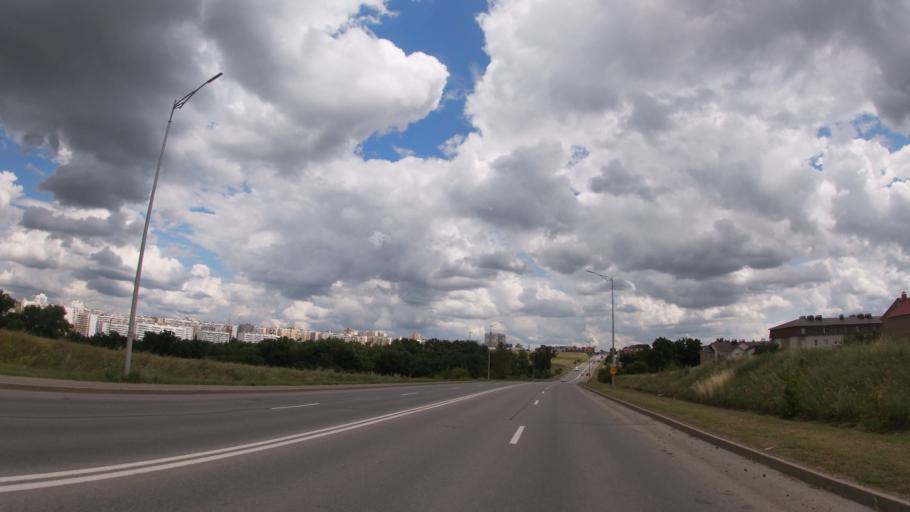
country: RU
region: Belgorod
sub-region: Belgorodskiy Rayon
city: Belgorod
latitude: 50.5505
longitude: 36.5481
